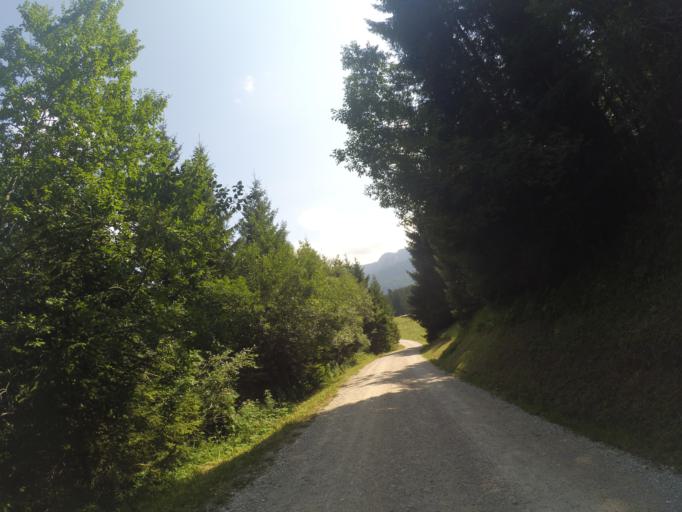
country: DE
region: Bavaria
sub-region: Swabia
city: Halblech
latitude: 47.6055
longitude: 10.8179
